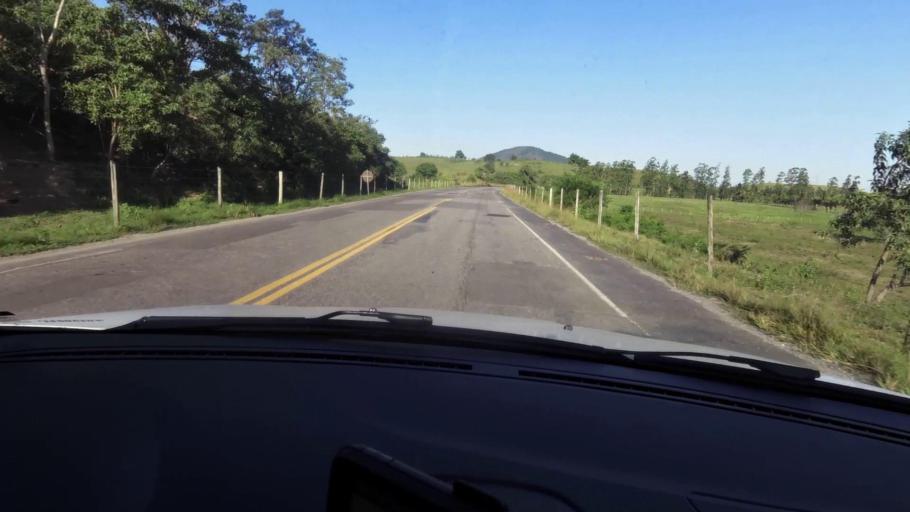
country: BR
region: Espirito Santo
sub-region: Alfredo Chaves
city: Alfredo Chaves
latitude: -20.7243
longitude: -40.6580
